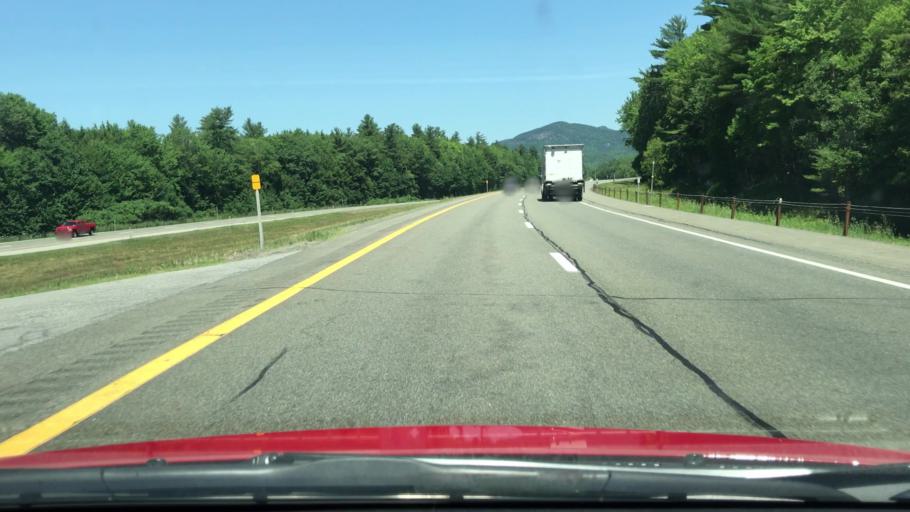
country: US
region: New York
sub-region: Essex County
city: Elizabethtown
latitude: 44.3348
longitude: -73.5333
